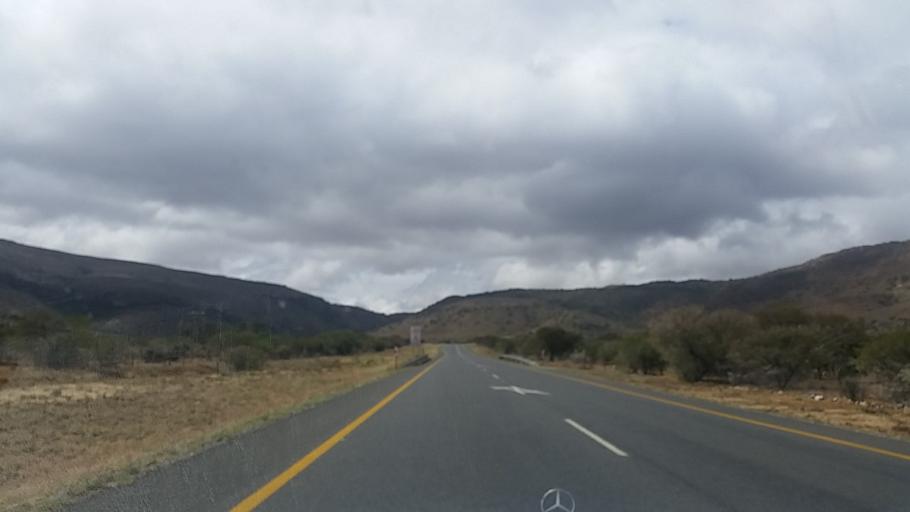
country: ZA
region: Eastern Cape
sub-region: Cacadu District Municipality
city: Graaff-Reinet
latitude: -31.9791
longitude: 24.7029
